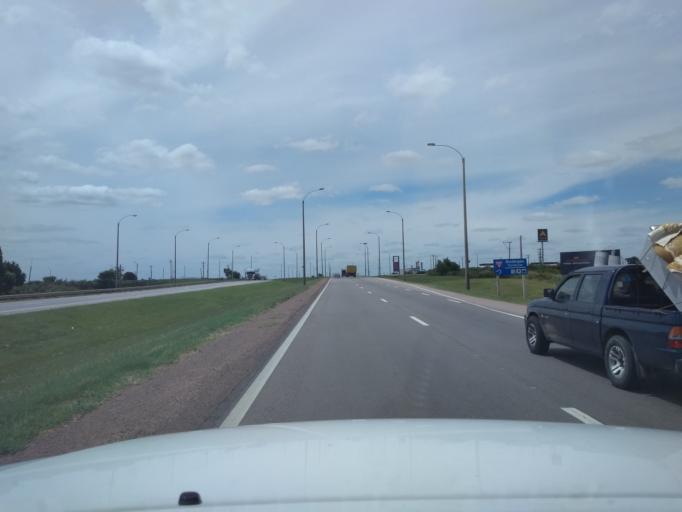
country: UY
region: Canelones
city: La Paz
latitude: -34.7528
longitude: -56.2568
